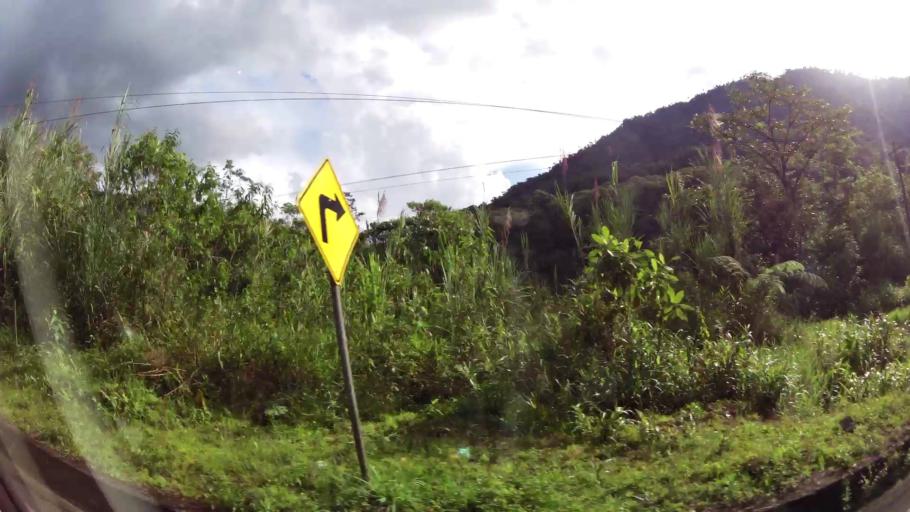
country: EC
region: Pastaza
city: Puyo
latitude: -1.4161
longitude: -78.1790
